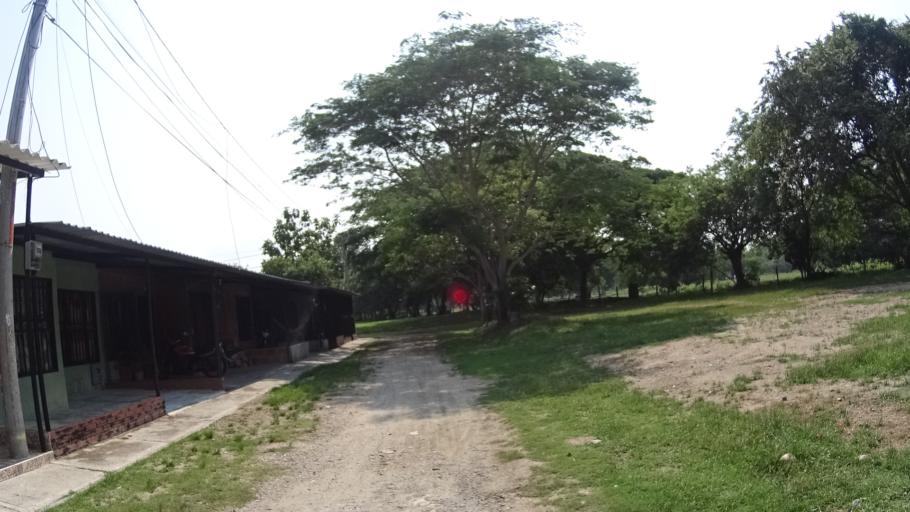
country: CO
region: Cundinamarca
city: Puerto Salgar
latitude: 5.4878
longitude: -74.6727
